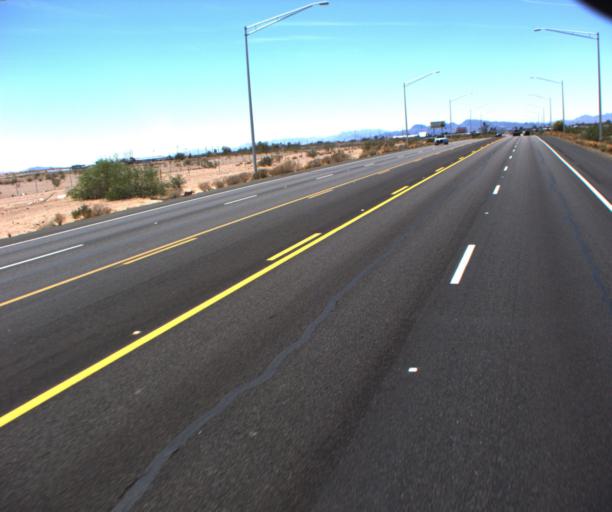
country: US
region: Arizona
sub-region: La Paz County
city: Parker
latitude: 34.1594
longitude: -114.2681
